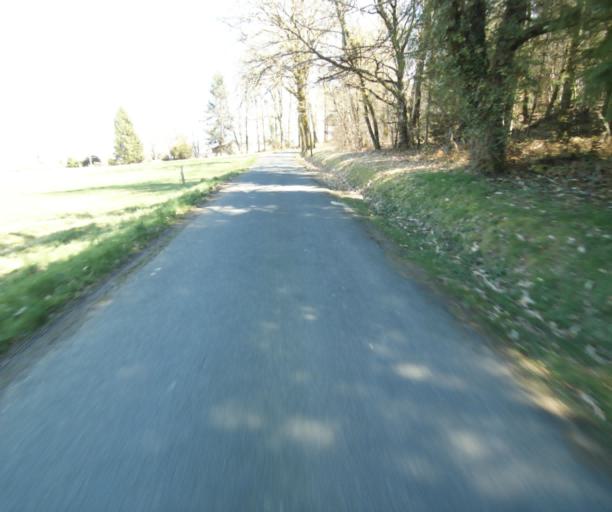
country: FR
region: Limousin
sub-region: Departement de la Correze
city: Chameyrat
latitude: 45.2742
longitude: 1.7029
